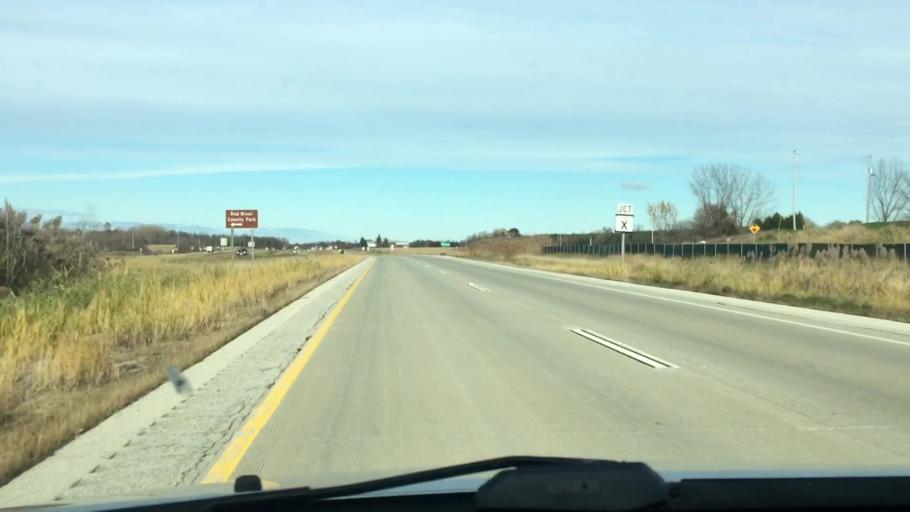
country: US
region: Wisconsin
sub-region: Kewaunee County
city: Luxemburg
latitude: 44.6561
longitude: -87.7485
